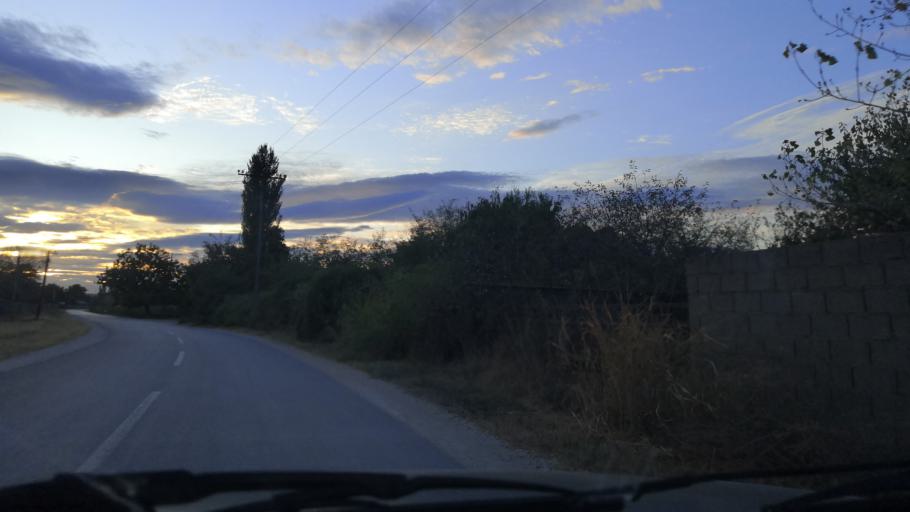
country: RO
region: Mehedinti
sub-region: Comuna Gogosu
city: Balta Verde
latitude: 44.2905
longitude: 22.6067
